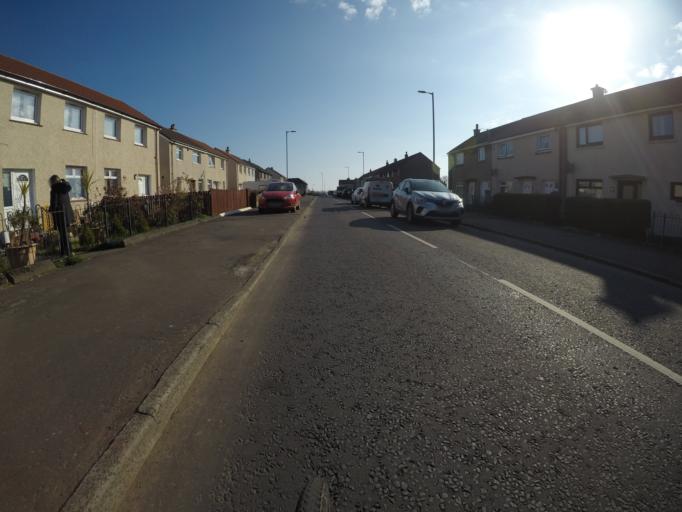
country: GB
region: Scotland
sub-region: North Ayrshire
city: Stevenston
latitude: 55.6481
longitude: -4.7457
